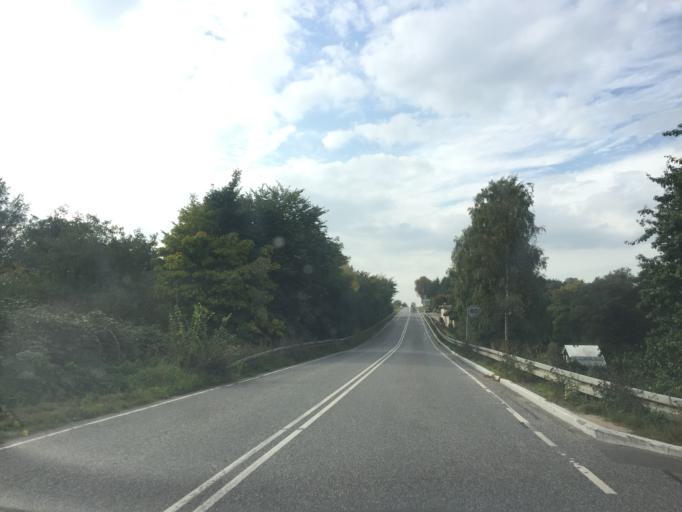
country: DK
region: Zealand
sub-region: Vordingborg Kommune
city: Praesto
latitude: 55.1646
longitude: 11.9696
